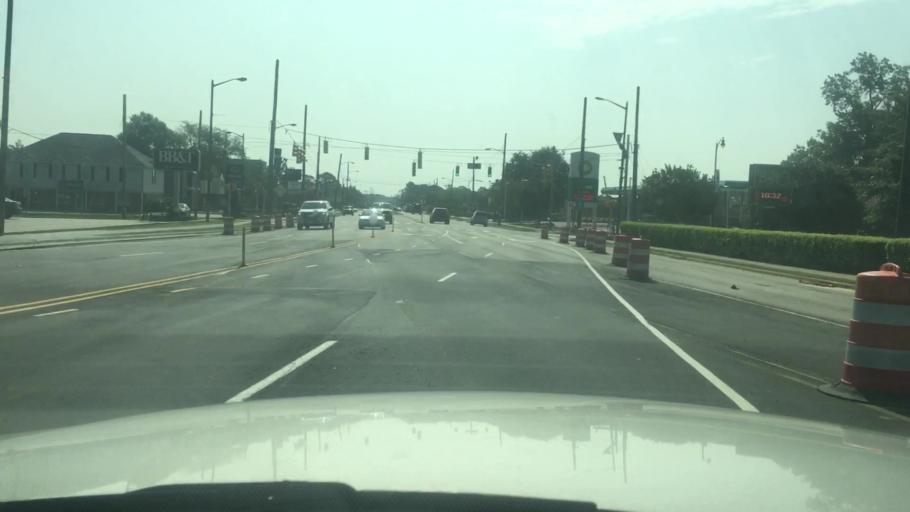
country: US
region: North Carolina
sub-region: Cumberland County
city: Fayetteville
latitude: 35.0587
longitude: -78.8811
